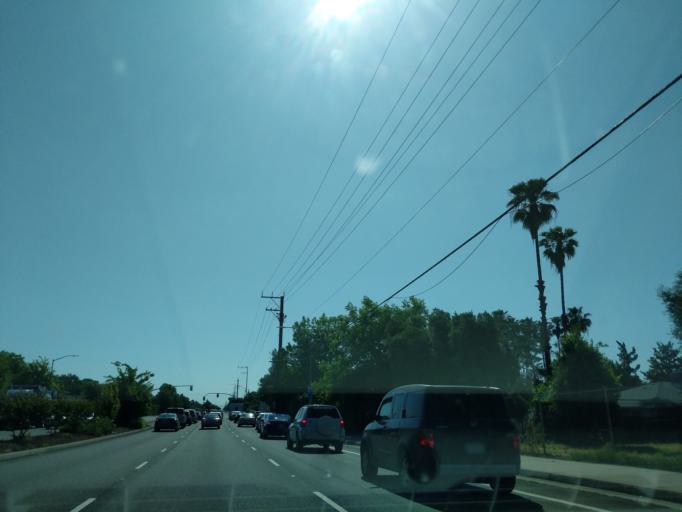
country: US
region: California
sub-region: Sacramento County
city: Antelope
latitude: 38.6781
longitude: -121.3124
